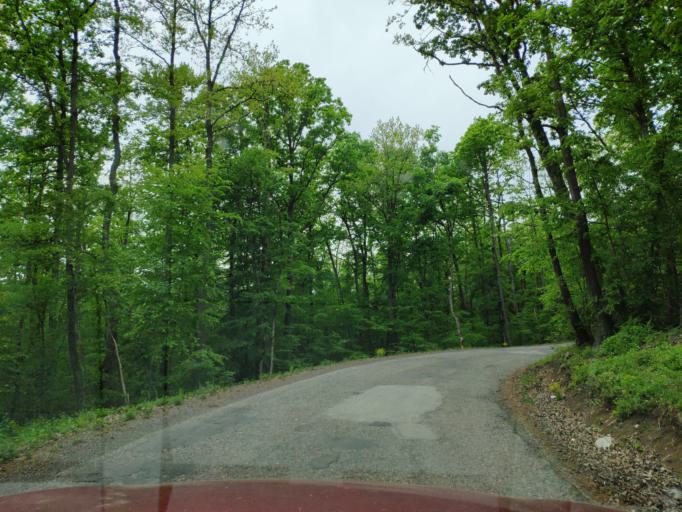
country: SK
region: Banskobystricky
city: Rimavska Sobota
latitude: 48.5195
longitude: 20.1064
